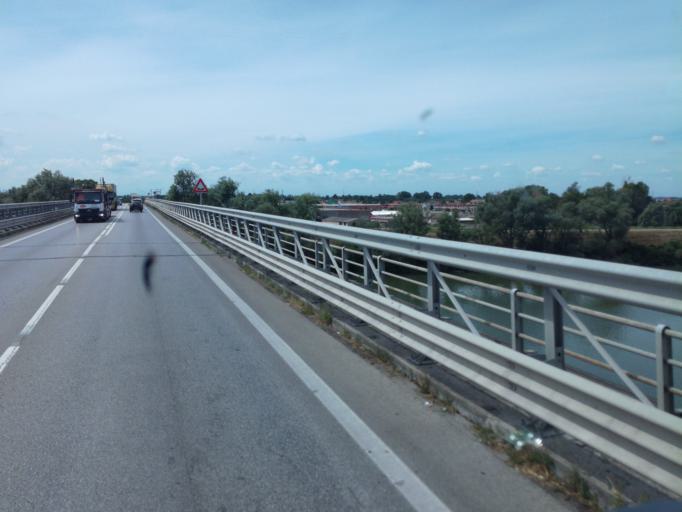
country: IT
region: Veneto
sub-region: Provincia di Rovigo
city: Taglio di Po
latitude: 45.0086
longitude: 12.2271
